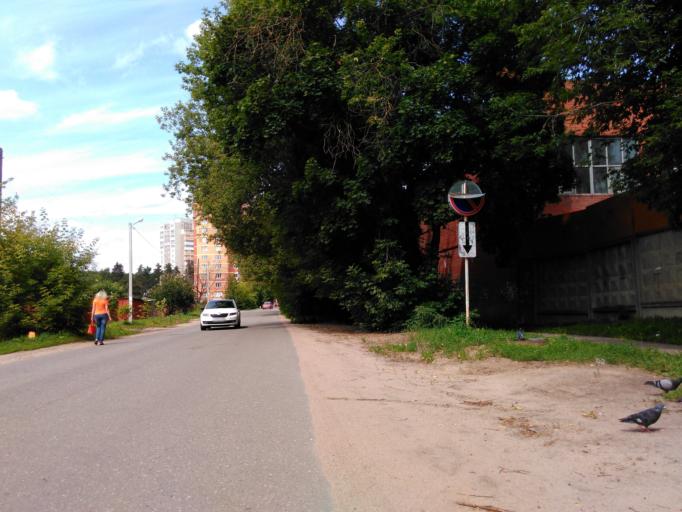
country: RU
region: Moskovskaya
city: Pravdinskiy
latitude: 56.0597
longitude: 37.8511
